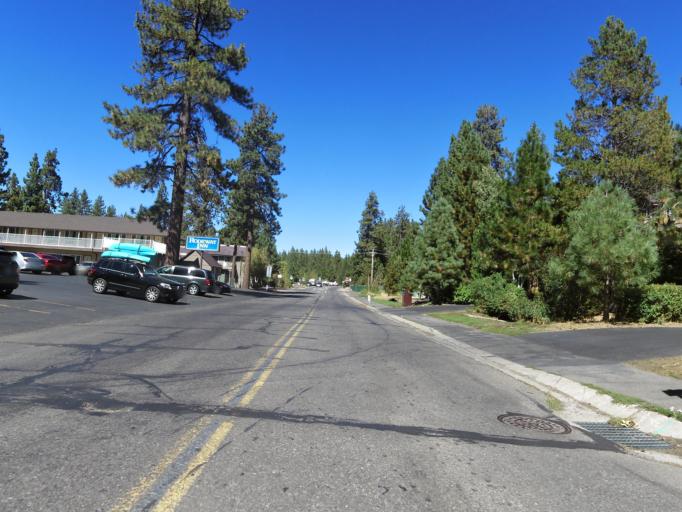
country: US
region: Nevada
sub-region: Douglas County
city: Kingsbury
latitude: 38.9601
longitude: -119.9468
